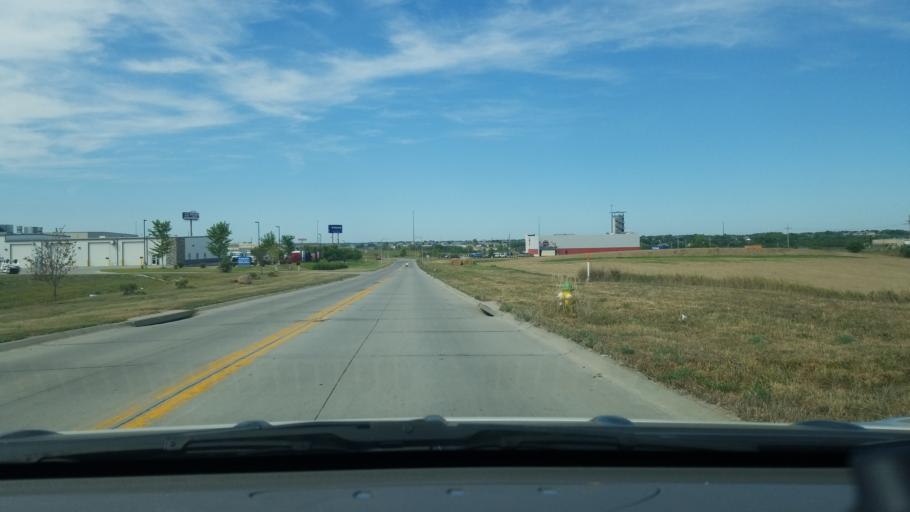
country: US
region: Nebraska
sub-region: Sarpy County
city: Chalco
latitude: 41.1456
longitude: -96.1511
